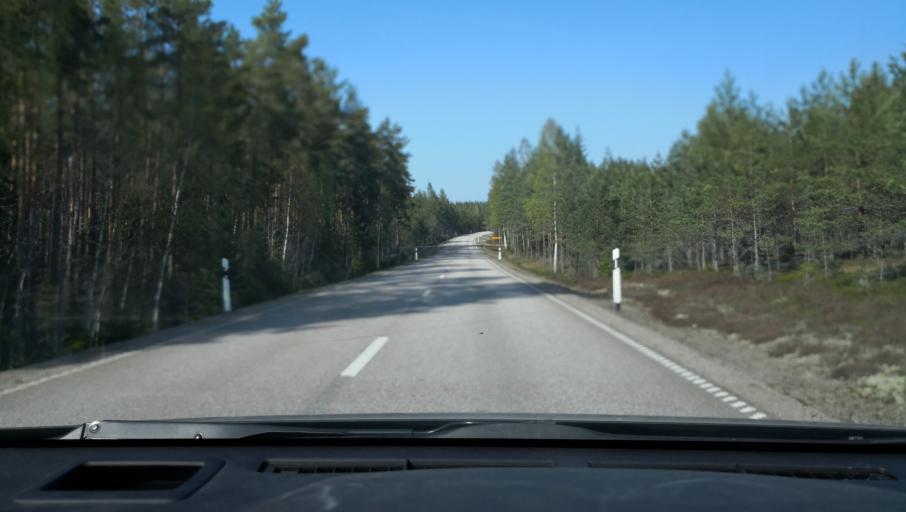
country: SE
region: Uppsala
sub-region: Heby Kommun
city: Tarnsjo
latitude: 60.0641
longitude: 16.8718
